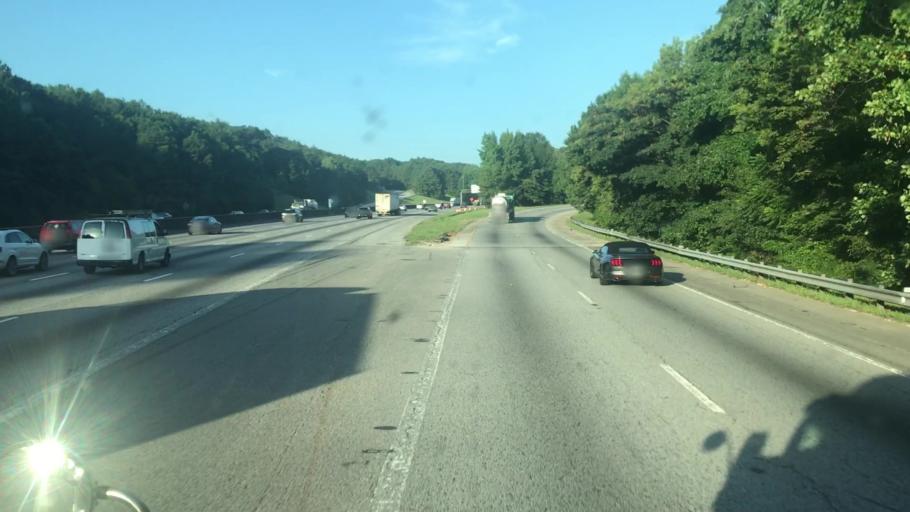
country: US
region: Georgia
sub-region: DeKalb County
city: Gresham Park
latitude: 33.6775
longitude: -84.3190
